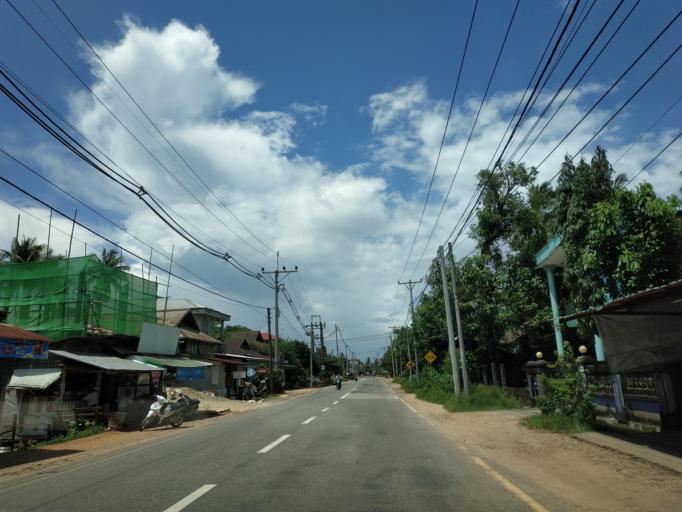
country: MM
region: Tanintharyi
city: Dawei
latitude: 14.0989
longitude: 98.1957
